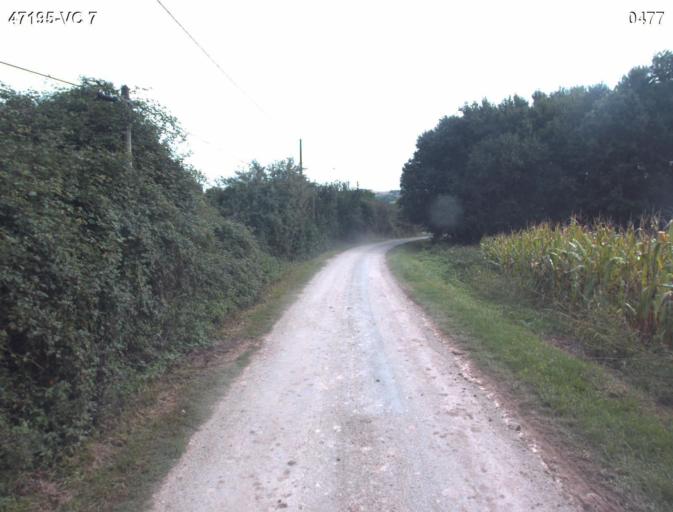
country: FR
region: Aquitaine
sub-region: Departement du Lot-et-Garonne
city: Nerac
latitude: 44.1084
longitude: 0.3494
